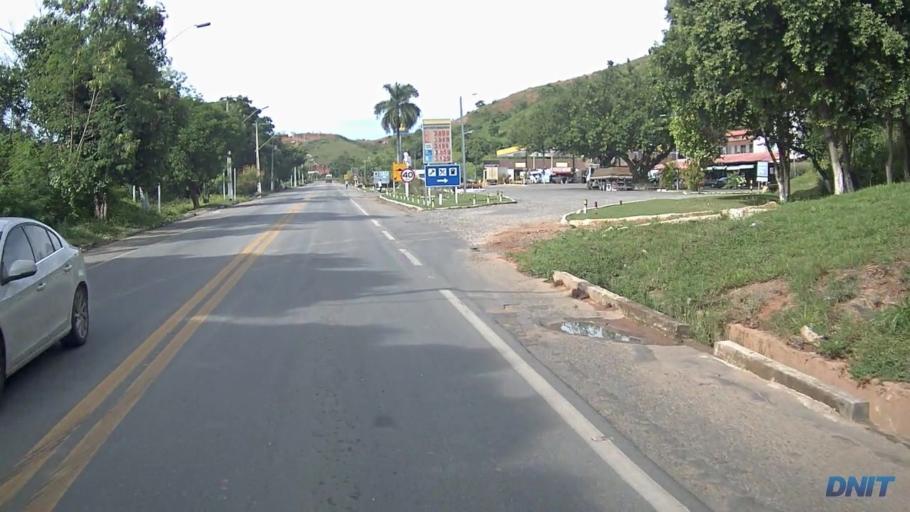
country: BR
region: Minas Gerais
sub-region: Belo Oriente
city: Belo Oriente
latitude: -19.2257
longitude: -42.3250
